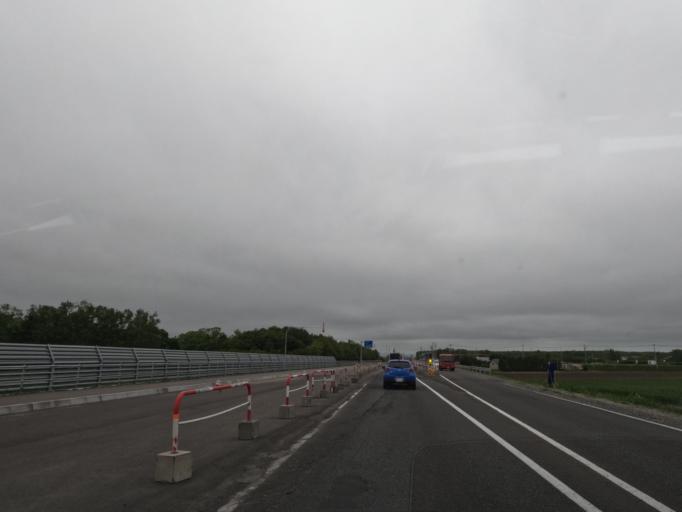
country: JP
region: Hokkaido
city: Ebetsu
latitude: 43.1428
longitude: 141.5166
